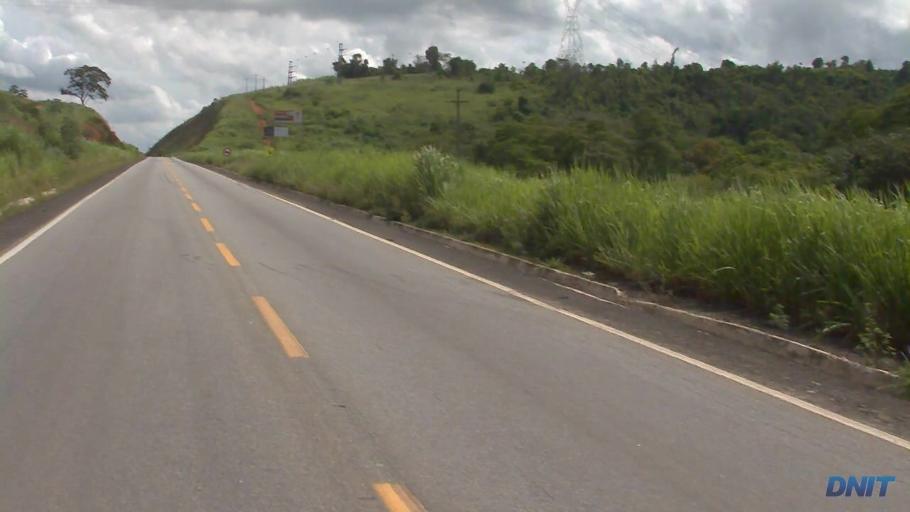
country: BR
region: Minas Gerais
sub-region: Ipatinga
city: Ipatinga
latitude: -19.4148
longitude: -42.4917
